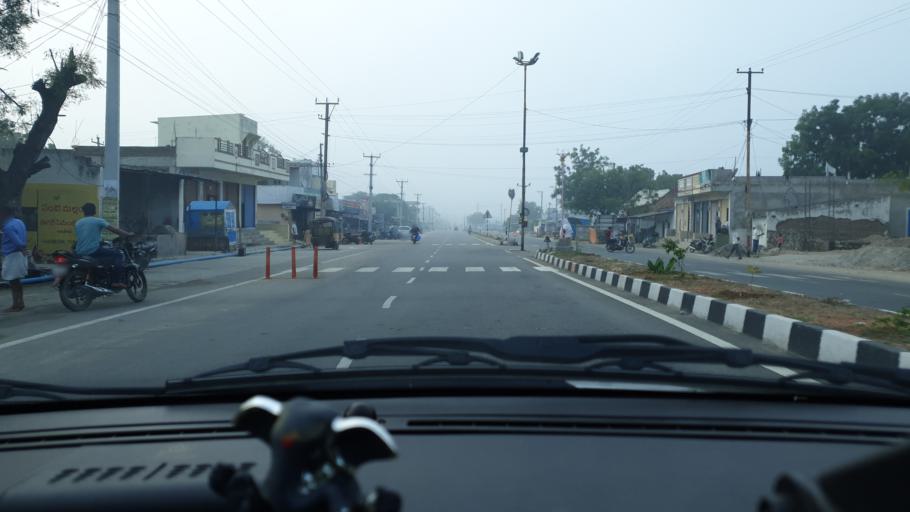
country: IN
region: Telangana
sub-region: Mahbubnagar
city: Farrukhnagar
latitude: 16.8811
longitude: 78.5292
